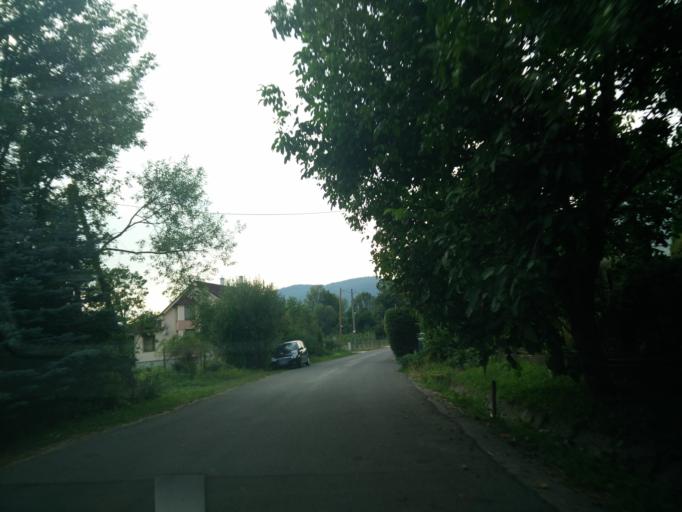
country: SK
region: Nitriansky
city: Handlova
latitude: 48.6502
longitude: 18.7884
